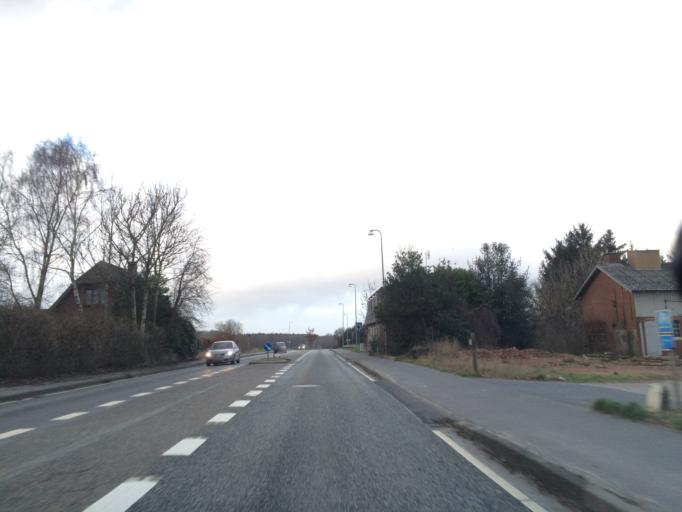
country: DK
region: Central Jutland
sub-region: Silkeborg Kommune
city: Virklund
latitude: 56.1079
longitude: 9.5741
